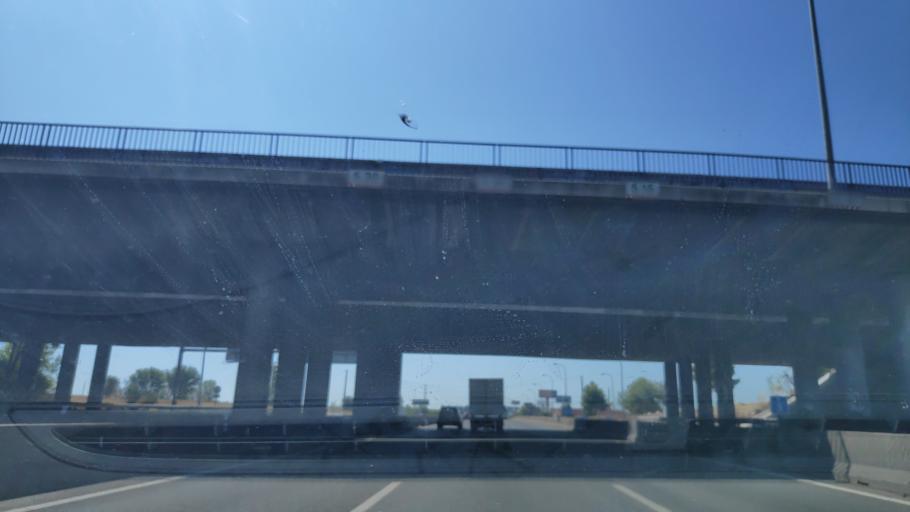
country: ES
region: Madrid
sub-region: Provincia de Madrid
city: Villaverde
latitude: 40.3651
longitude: -3.7208
